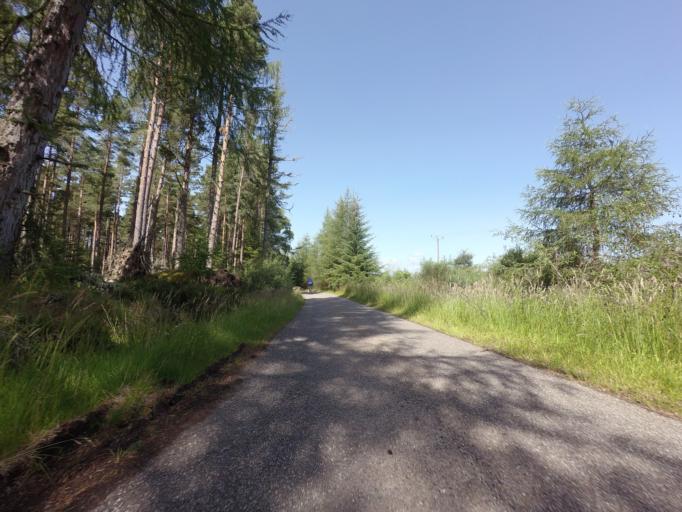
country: GB
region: Scotland
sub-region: Highland
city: Nairn
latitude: 57.4996
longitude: -3.9703
